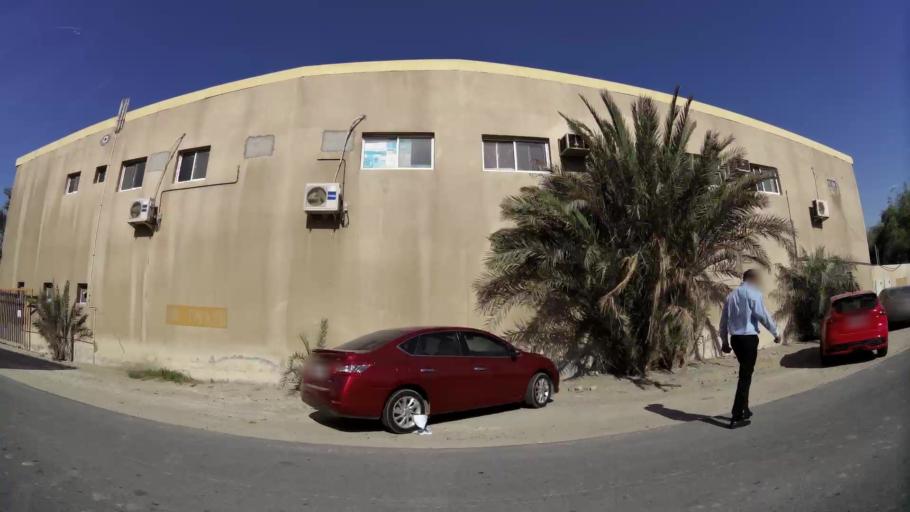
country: AE
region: Dubai
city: Dubai
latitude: 24.9874
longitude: 55.1054
